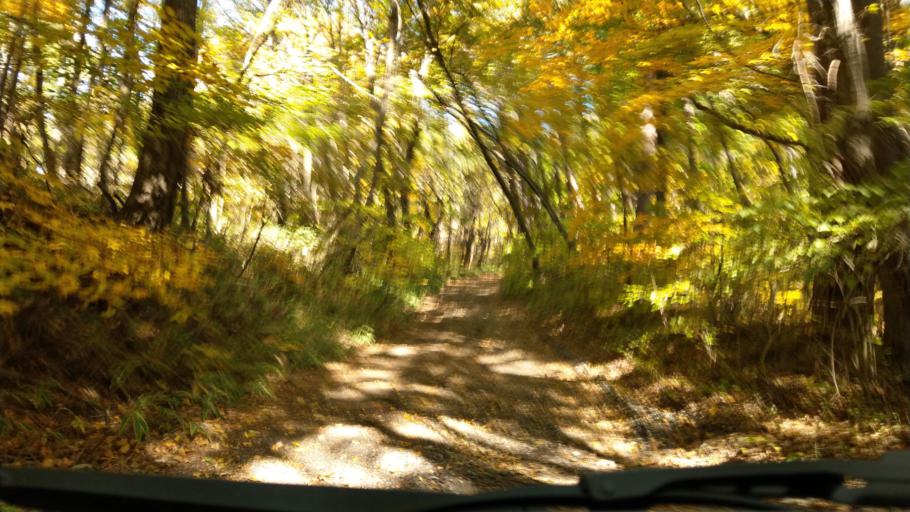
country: JP
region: Nagano
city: Komoro
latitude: 36.3651
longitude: 138.4525
